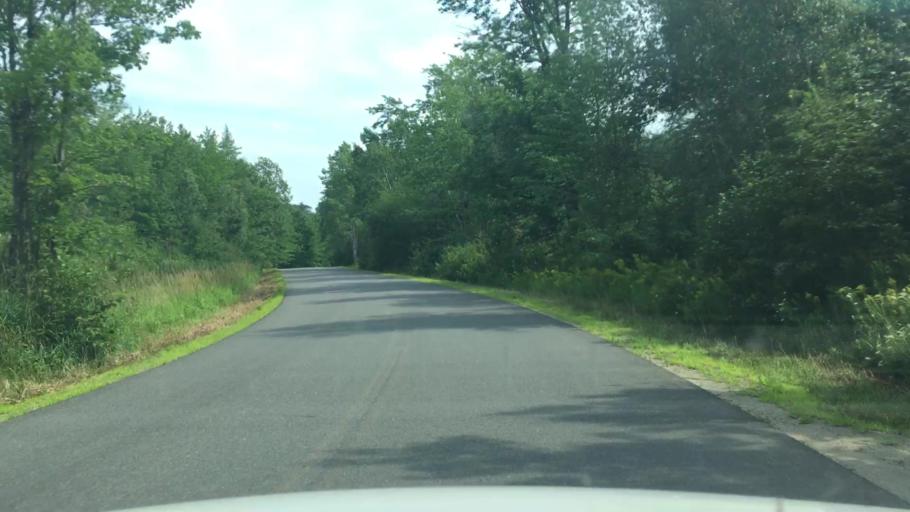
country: US
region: Maine
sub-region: Lincoln County
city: Jefferson
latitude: 44.2495
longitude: -69.4468
